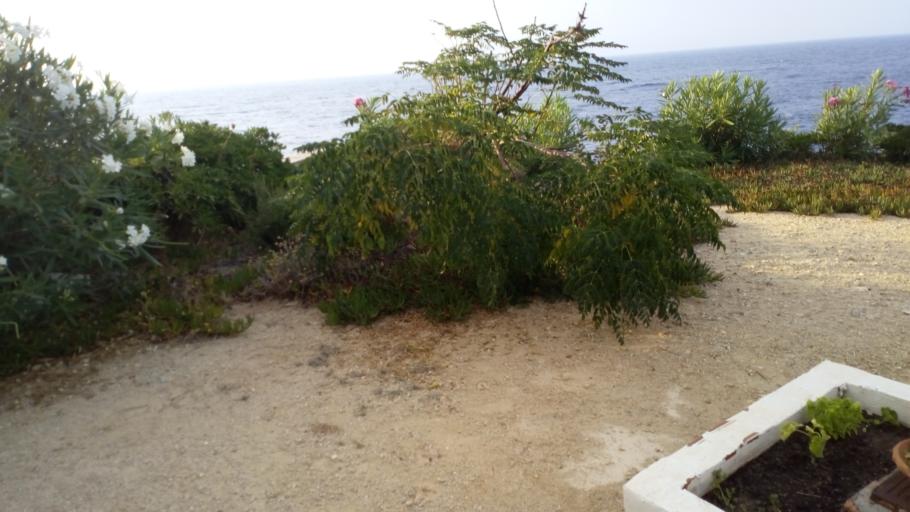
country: GR
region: North Aegean
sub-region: Nomos Samou
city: Agios Kirykos
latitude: 37.6351
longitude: 26.0850
